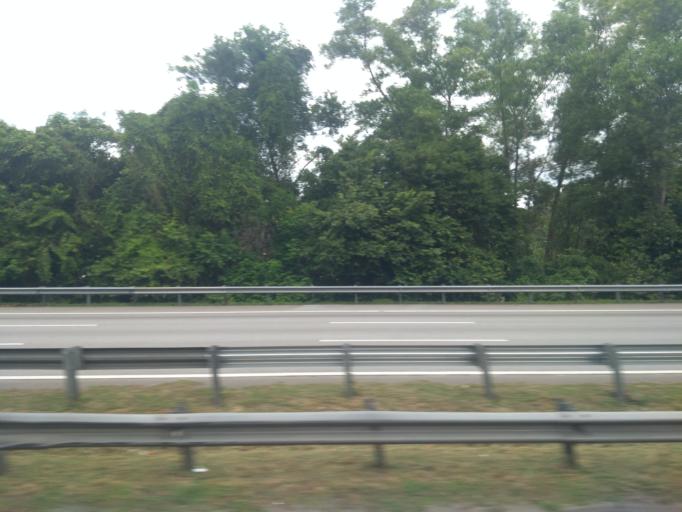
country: MY
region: Melaka
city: Pulau Sebang
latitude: 2.4432
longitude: 102.1954
